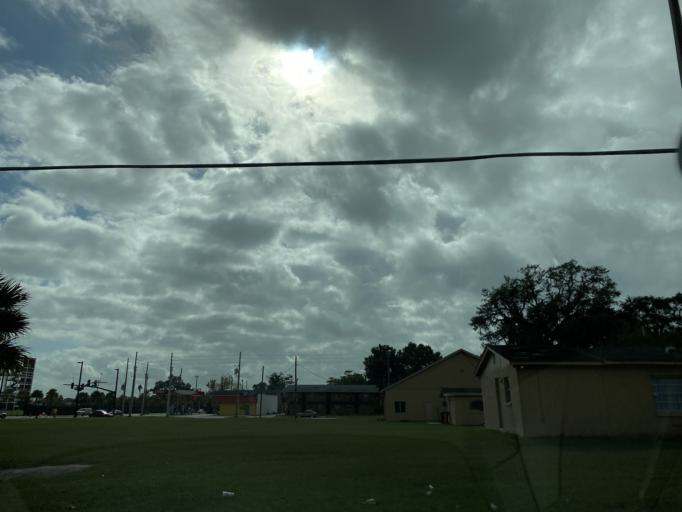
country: US
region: Florida
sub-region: Orange County
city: Orlando
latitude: 28.5411
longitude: -81.4063
